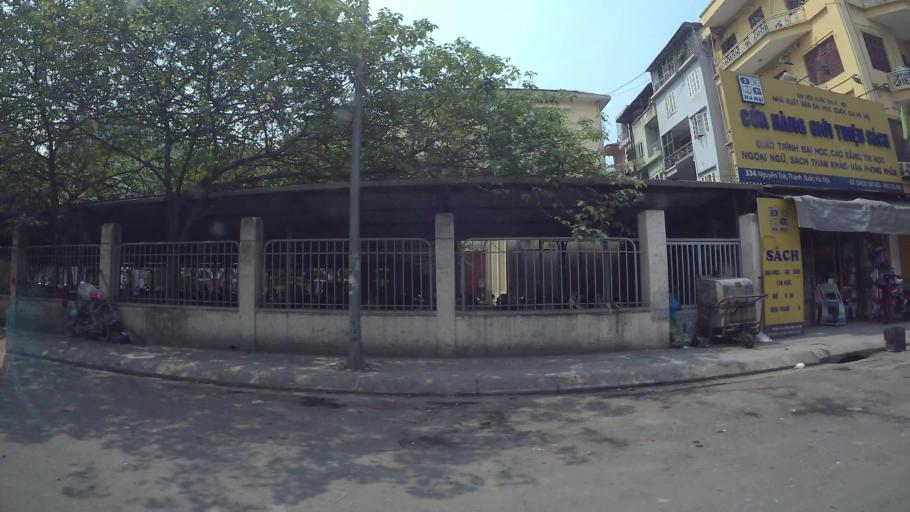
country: VN
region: Ha Noi
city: Thanh Xuan
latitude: 20.9959
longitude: 105.8087
